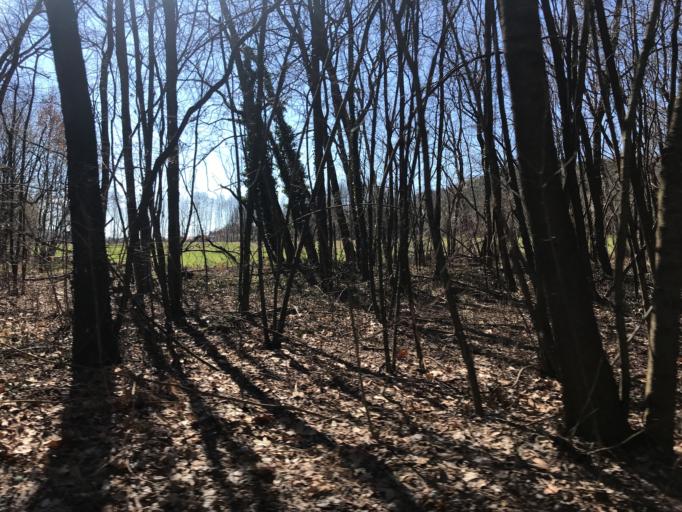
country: IT
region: Lombardy
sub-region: Provincia di Varese
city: Ranco
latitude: 45.7929
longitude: 8.5925
